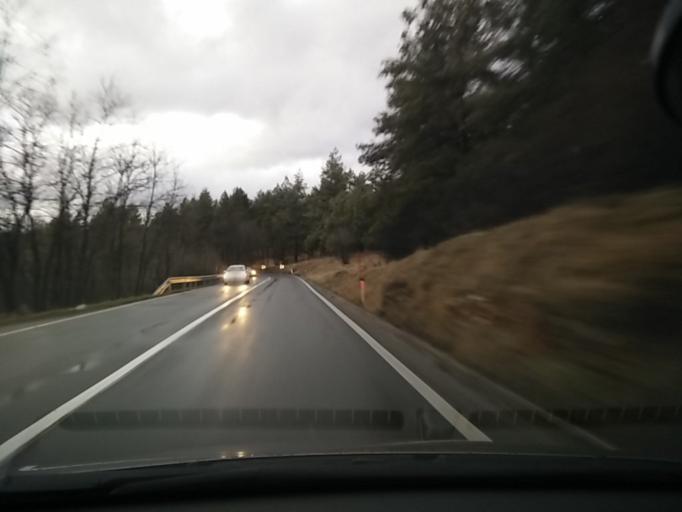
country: SI
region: Pivka
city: Pivka
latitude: 45.5273
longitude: 14.1305
